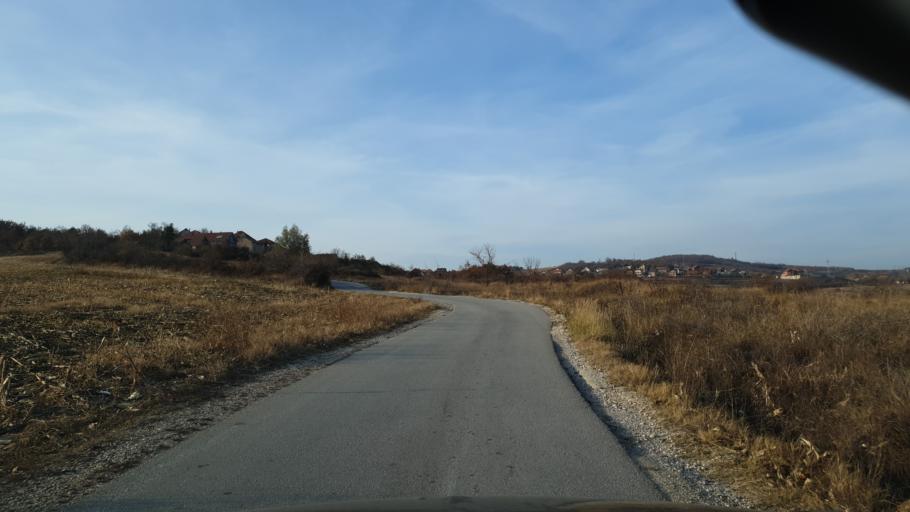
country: RS
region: Central Serbia
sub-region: Borski Okrug
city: Bor
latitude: 44.0503
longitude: 22.0919
